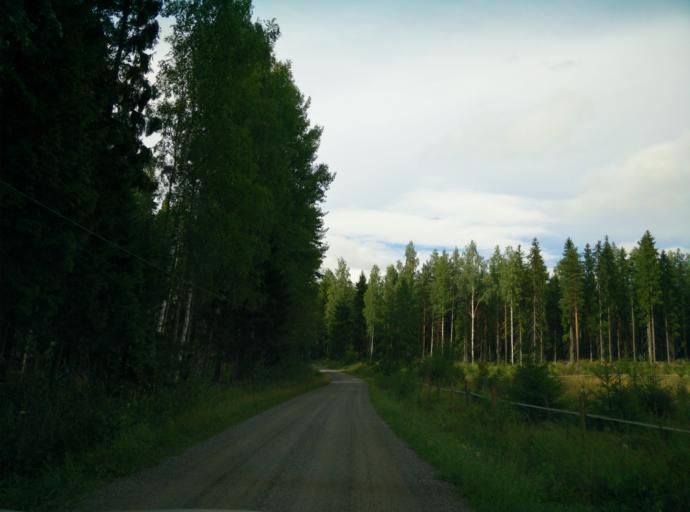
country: FI
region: Haeme
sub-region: Haemeenlinna
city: Kalvola
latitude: 61.1256
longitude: 24.1403
